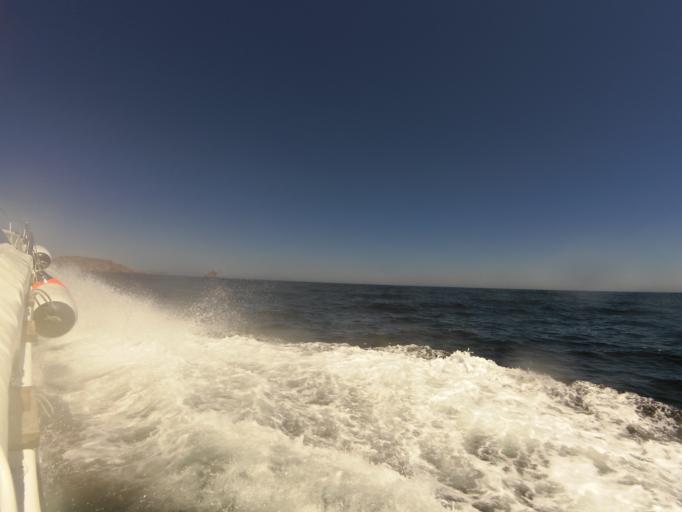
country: PT
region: Leiria
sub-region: Peniche
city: Peniche
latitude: 39.4004
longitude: -9.4876
